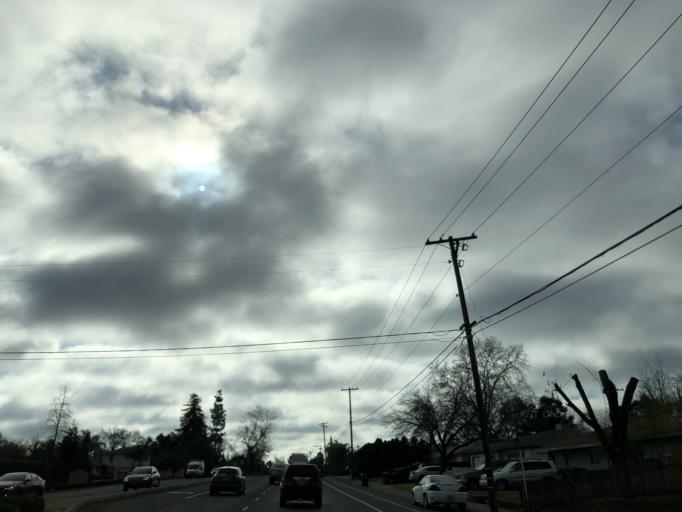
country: US
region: California
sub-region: Sacramento County
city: Arden-Arcade
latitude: 38.5908
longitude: -121.3831
